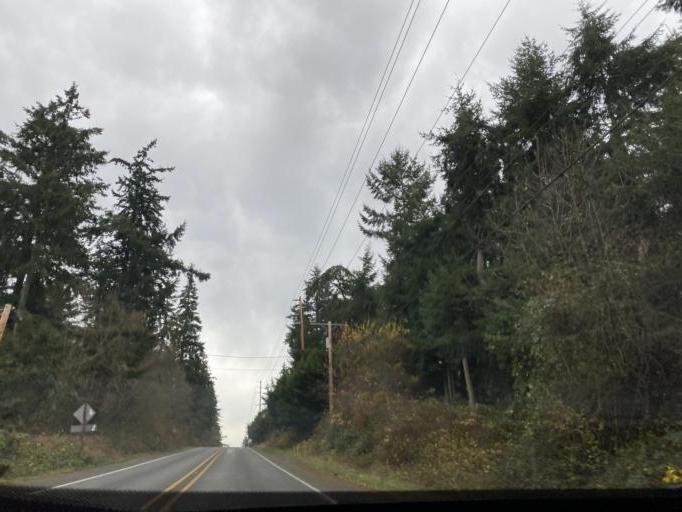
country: US
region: Washington
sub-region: Island County
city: Freeland
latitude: 48.0145
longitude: -122.5602
